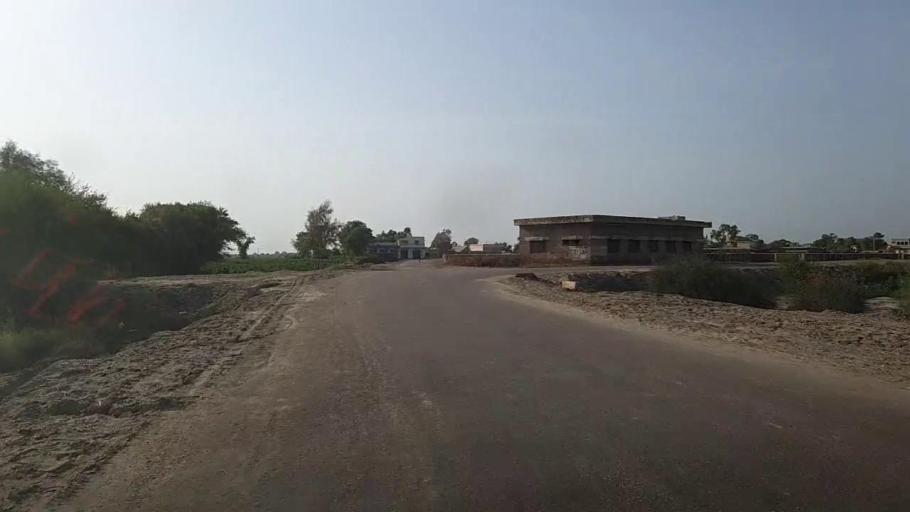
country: PK
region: Sindh
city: Ubauro
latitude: 28.1008
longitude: 69.8453
